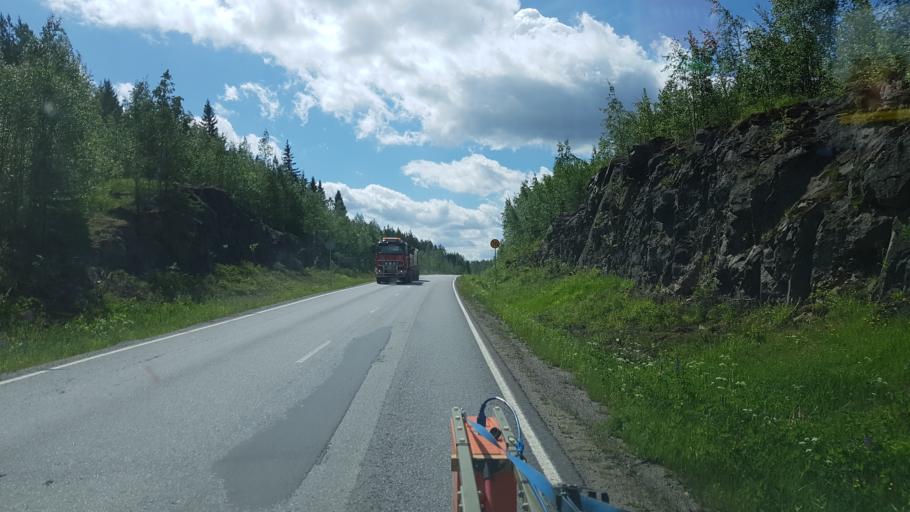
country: FI
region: Pirkanmaa
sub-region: Tampere
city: Pirkkala
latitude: 61.4077
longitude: 23.6336
